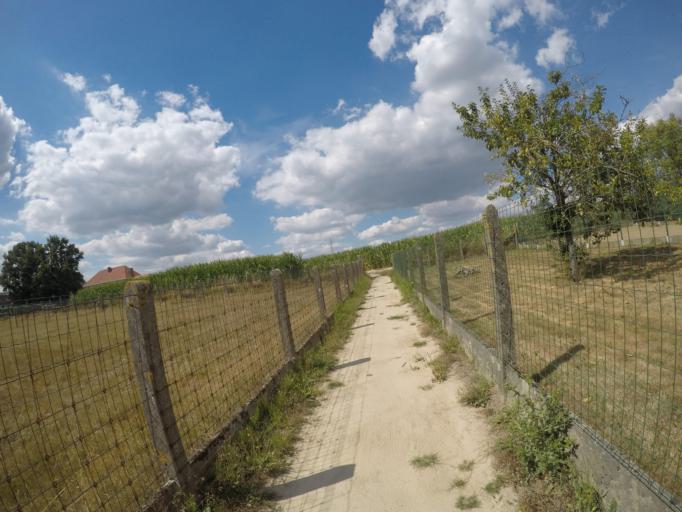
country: BE
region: Flanders
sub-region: Provincie Vlaams-Brabant
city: Ledeberg
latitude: 50.8502
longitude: 4.1242
